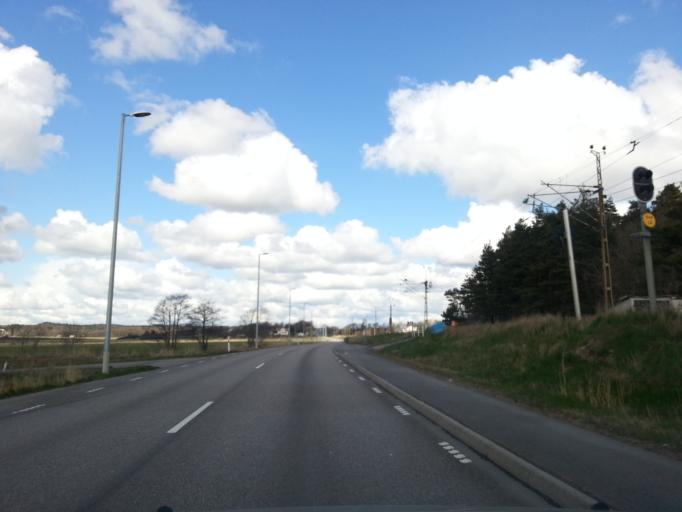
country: SE
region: Vaestra Goetaland
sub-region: Kungalvs Kommun
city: Kungalv
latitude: 57.8065
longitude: 11.9098
